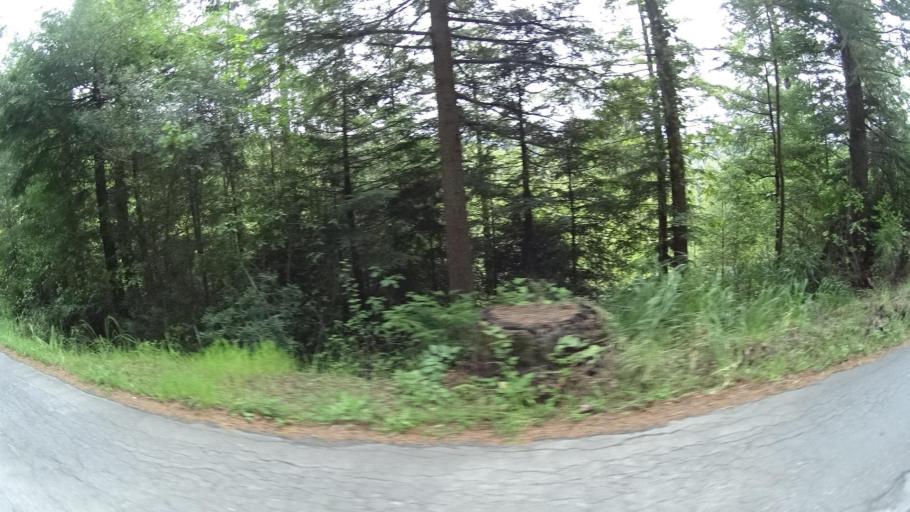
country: US
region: California
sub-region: Humboldt County
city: Bayside
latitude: 40.7863
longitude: -124.0676
